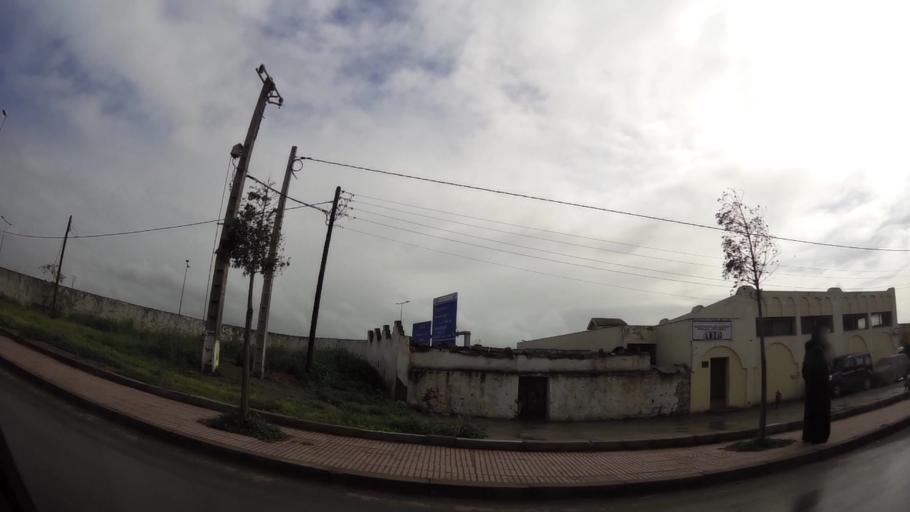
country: MA
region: Grand Casablanca
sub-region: Mohammedia
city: Mohammedia
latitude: 33.6358
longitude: -7.4460
